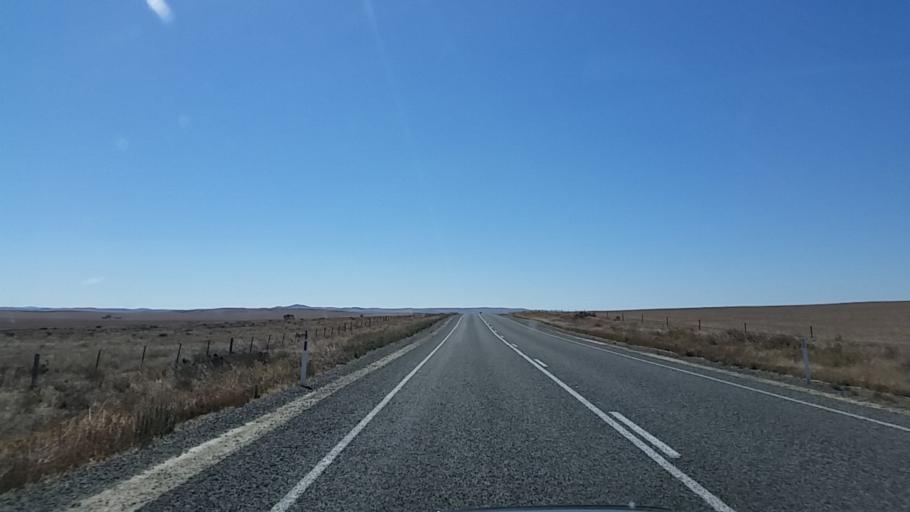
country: AU
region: South Australia
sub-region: Northern Areas
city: Jamestown
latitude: -33.2938
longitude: 138.8726
